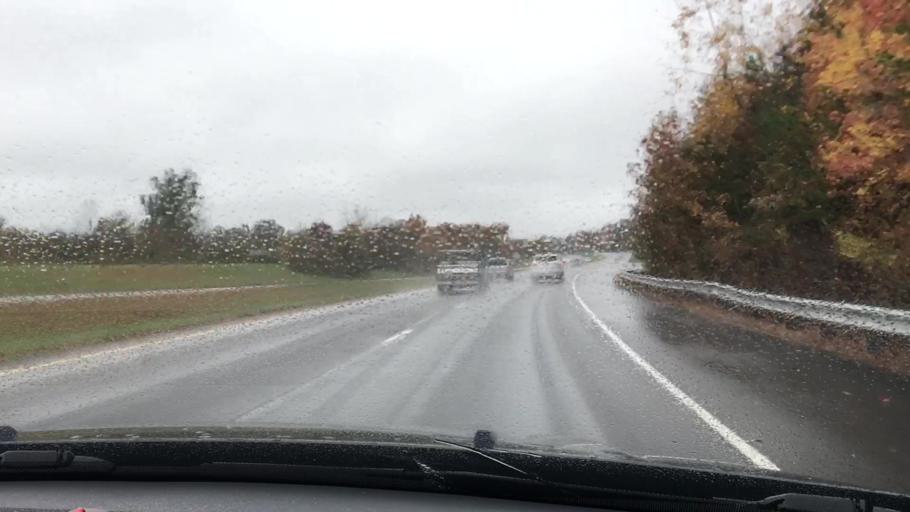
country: US
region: Virginia
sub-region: Prince William County
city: Lake Ridge
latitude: 38.7331
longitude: -77.2794
